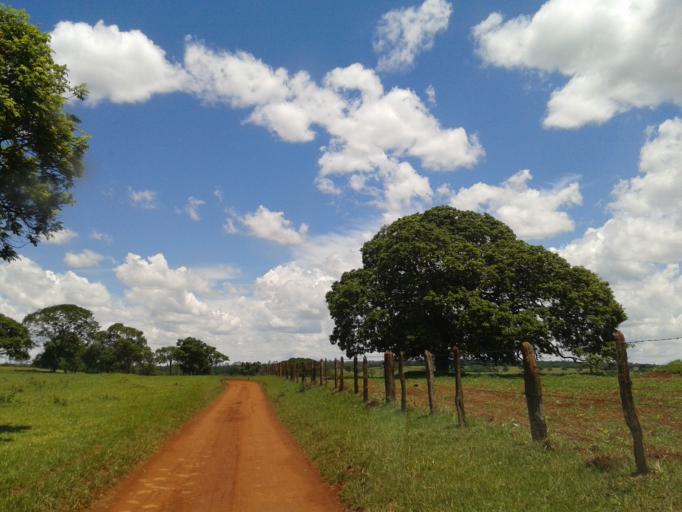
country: BR
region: Minas Gerais
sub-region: Centralina
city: Centralina
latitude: -18.6973
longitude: -49.1873
